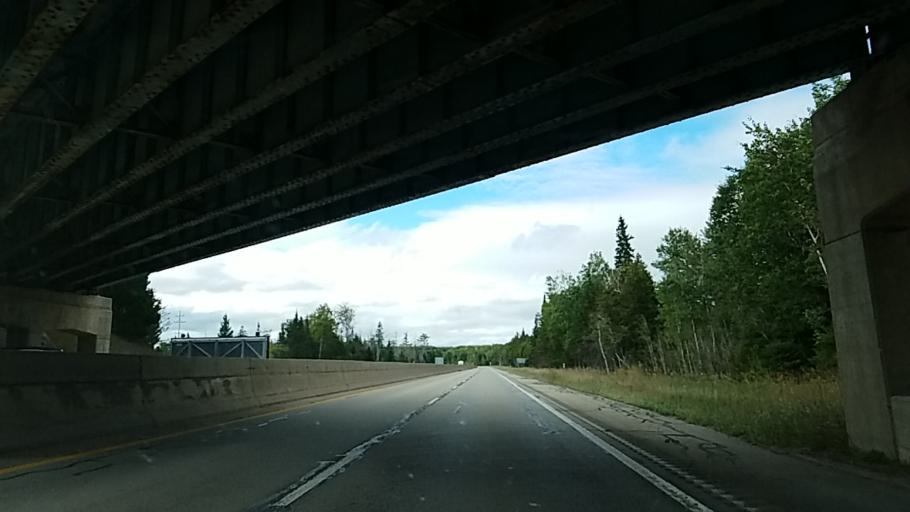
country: US
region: Michigan
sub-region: Mackinac County
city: Saint Ignace
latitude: 45.7725
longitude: -84.7346
